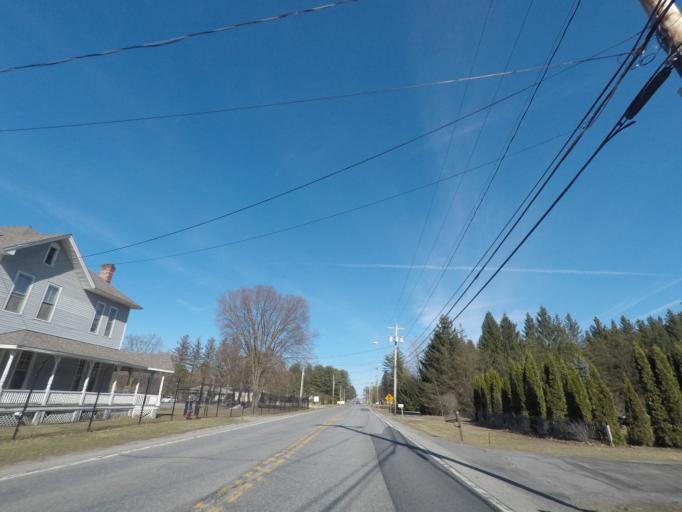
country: US
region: New York
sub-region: Saratoga County
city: Saratoga Springs
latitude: 43.0779
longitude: -73.8202
